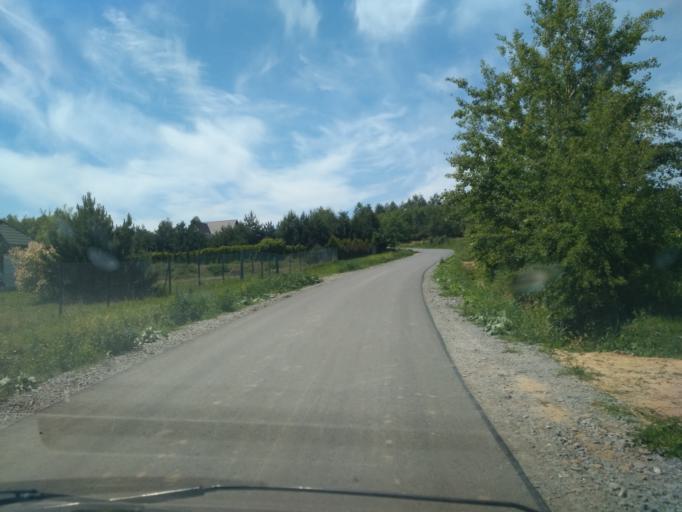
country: PL
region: Subcarpathian Voivodeship
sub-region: Powiat rzeszowski
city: Lubenia
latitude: 49.9201
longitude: 21.9212
